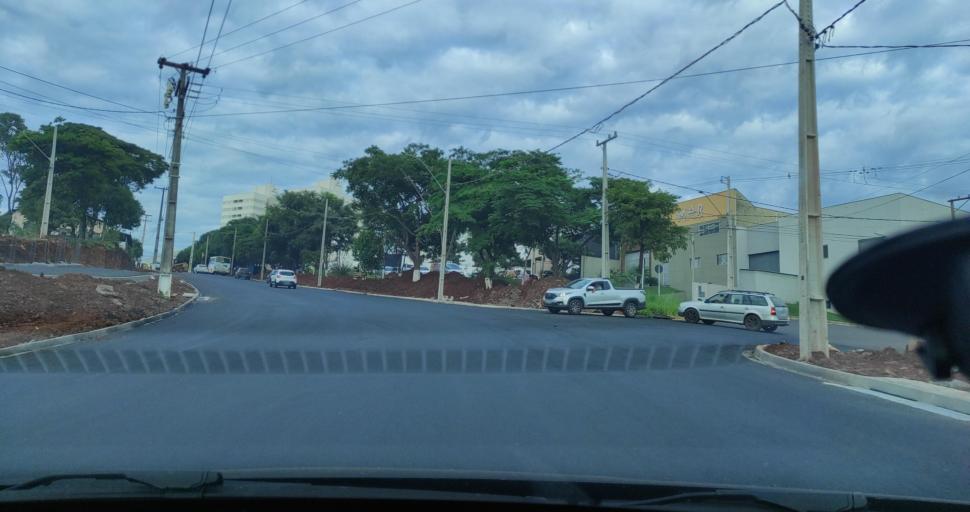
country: BR
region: Parana
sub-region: Ibipora
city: Ibipora
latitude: -23.2520
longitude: -51.0497
